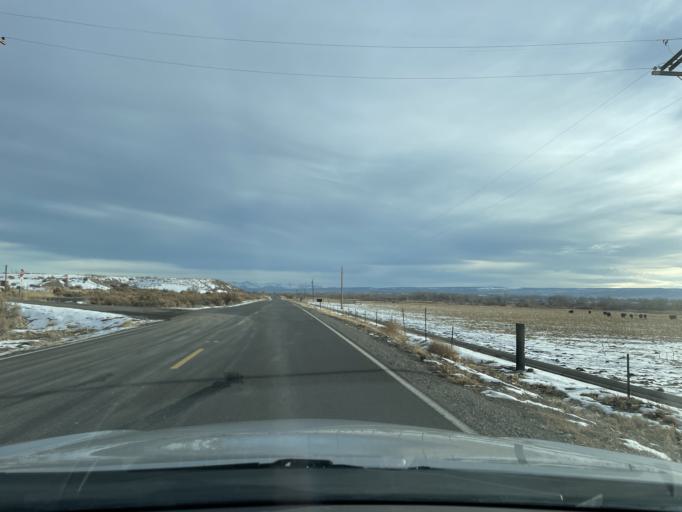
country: US
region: Colorado
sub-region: Montrose County
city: Olathe
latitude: 38.6570
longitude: -107.9973
